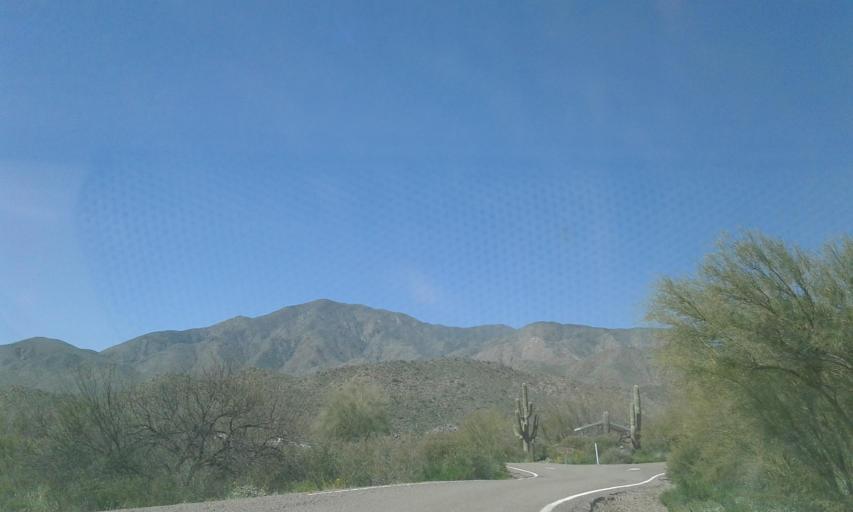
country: US
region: Arizona
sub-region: Gila County
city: Tonto Basin
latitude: 33.6261
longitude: -111.2032
